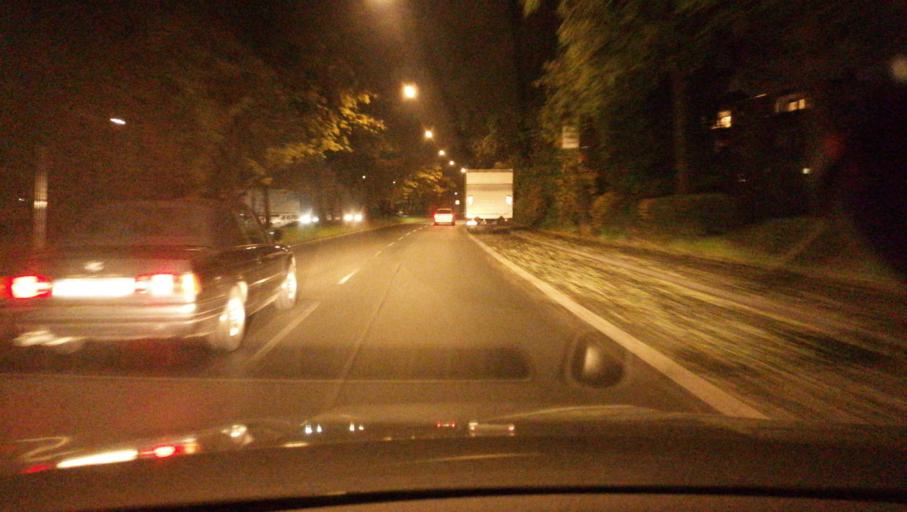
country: DE
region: North Rhine-Westphalia
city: Herten
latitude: 51.6059
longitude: 7.1696
